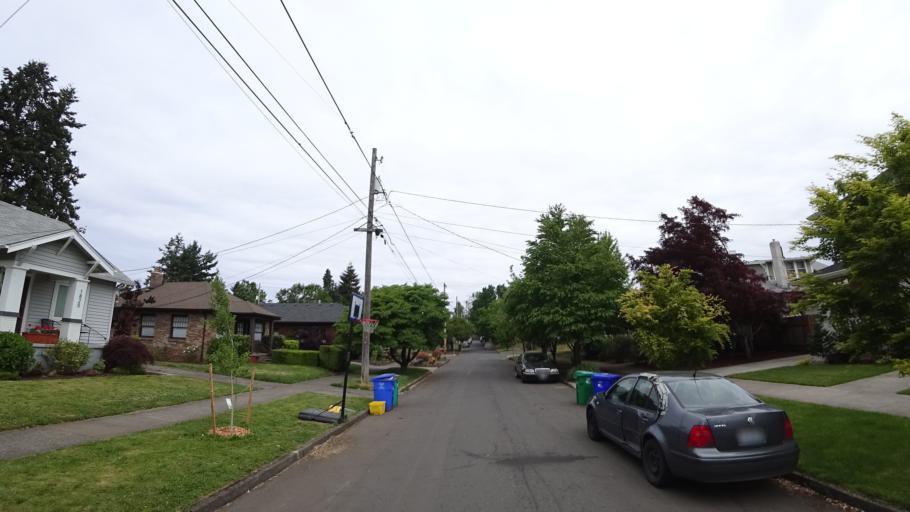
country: US
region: Oregon
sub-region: Multnomah County
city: Lents
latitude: 45.5360
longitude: -122.6059
